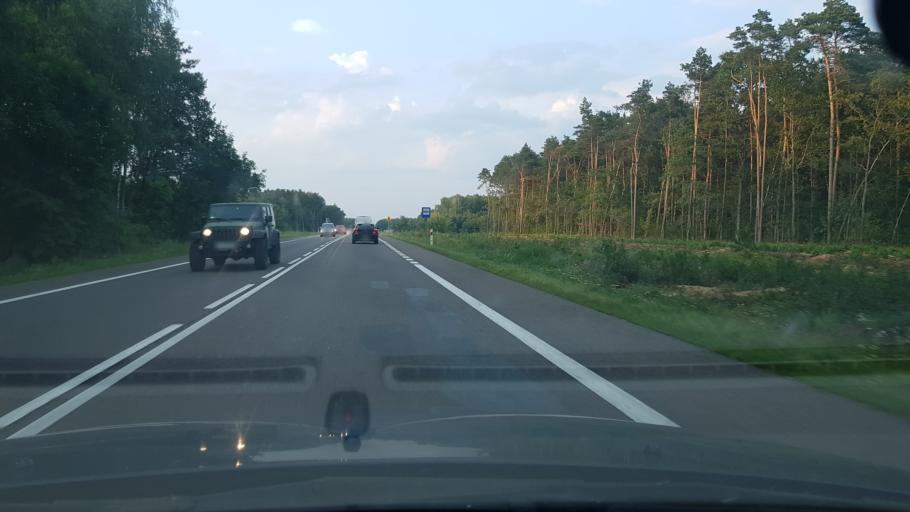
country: PL
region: Masovian Voivodeship
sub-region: Powiat ciechanowski
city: Glinojeck
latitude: 52.8381
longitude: 20.2690
